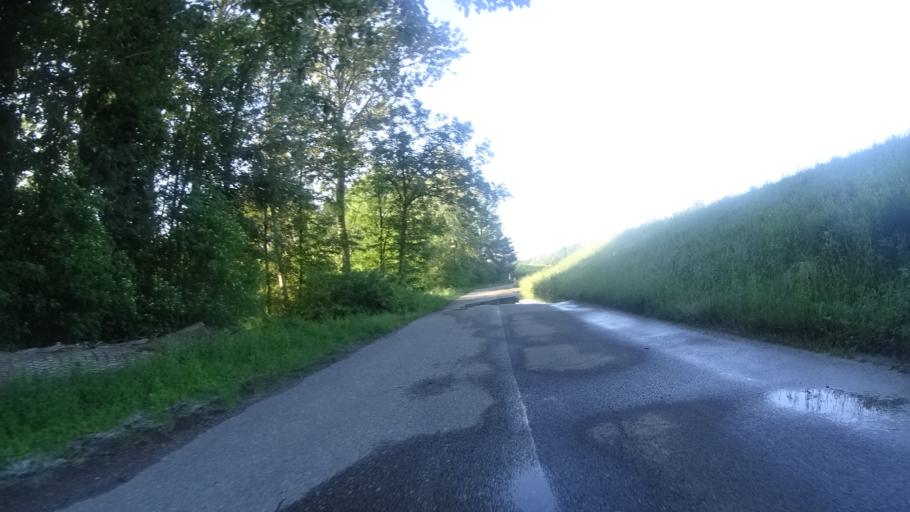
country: FR
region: Alsace
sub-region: Departement du Bas-Rhin
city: Drusenheim
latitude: 48.7440
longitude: 7.9711
